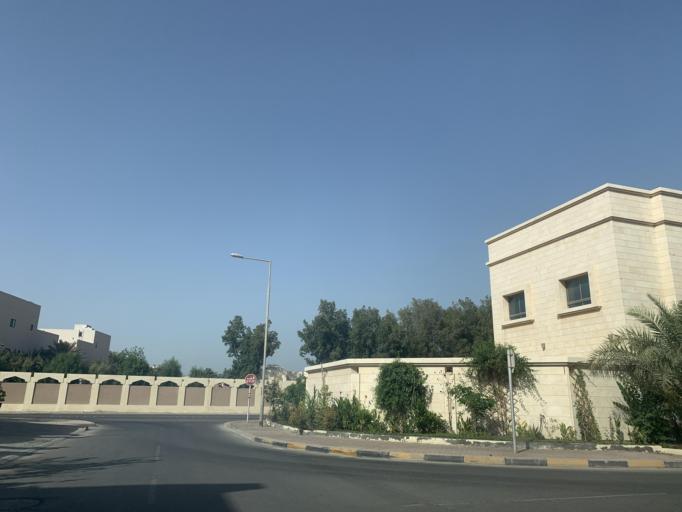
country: BH
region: Northern
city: Madinat `Isa
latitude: 26.1653
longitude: 50.5761
